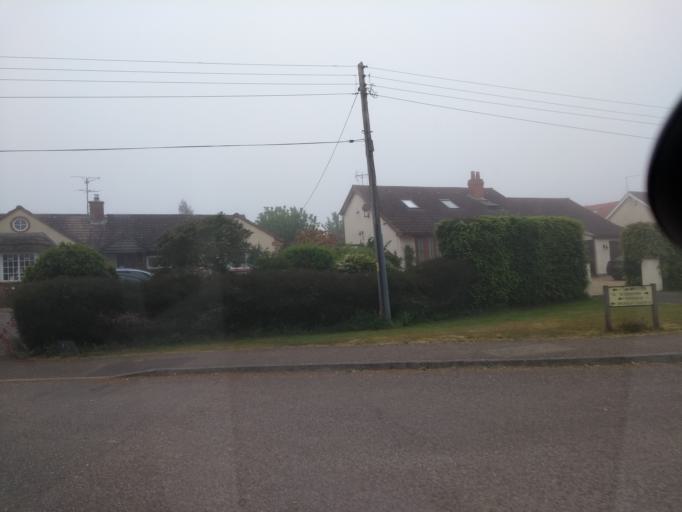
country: GB
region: England
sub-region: Somerset
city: Creech Saint Michael
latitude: 51.0389
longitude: -3.0654
